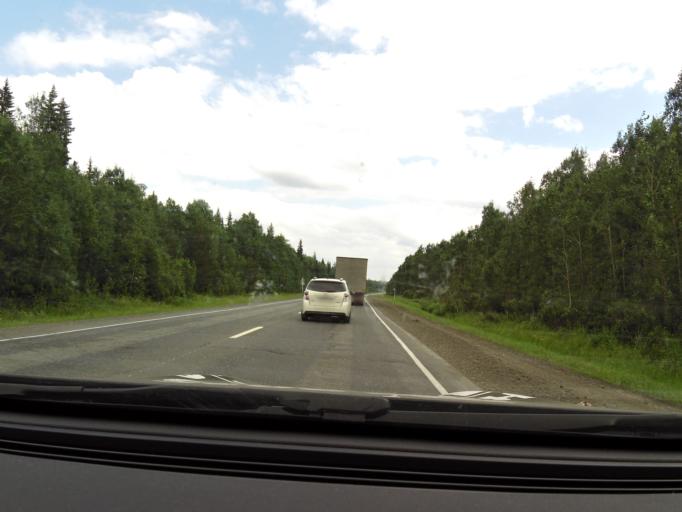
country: RU
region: Sverdlovsk
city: Atig
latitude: 56.8166
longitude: 59.3521
